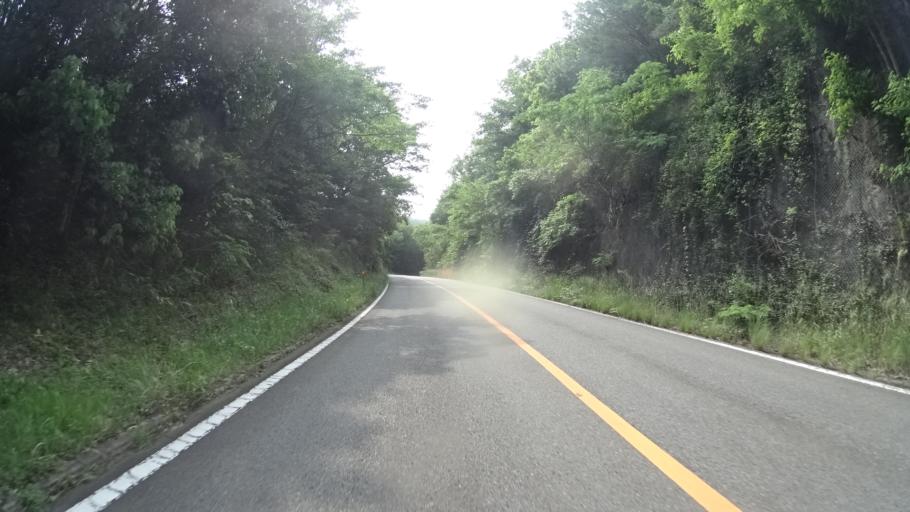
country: JP
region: Yamaguchi
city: Hagi
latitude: 34.2772
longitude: 131.3204
